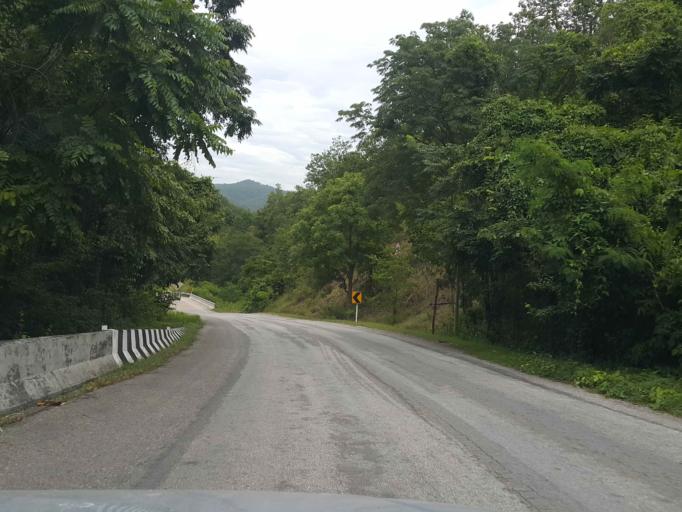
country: TH
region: Lampang
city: Thoen
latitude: 17.6404
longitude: 99.3062
